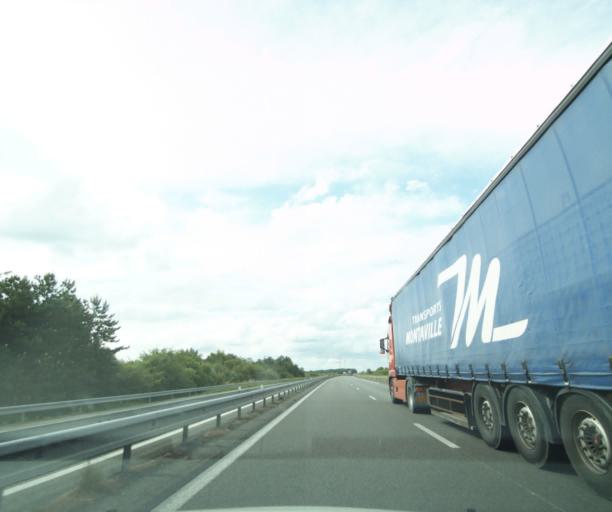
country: FR
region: Centre
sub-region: Departement du Cher
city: Mehun-sur-Yevre
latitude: 47.1207
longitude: 2.1936
